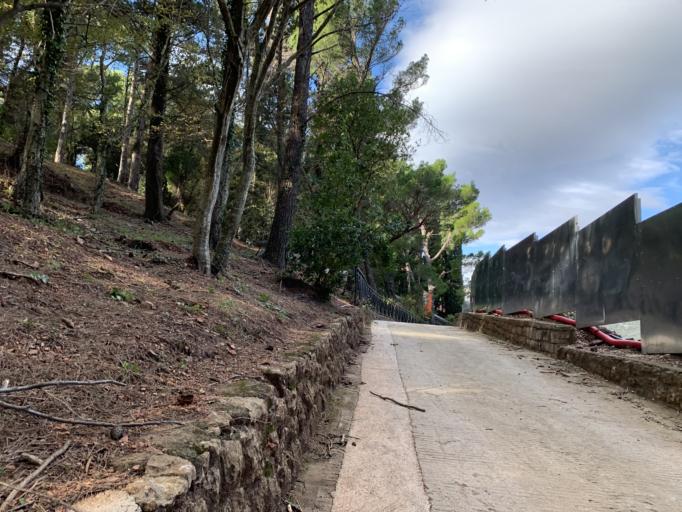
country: ME
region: Budva
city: Budva
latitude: 42.2649
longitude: 18.8923
